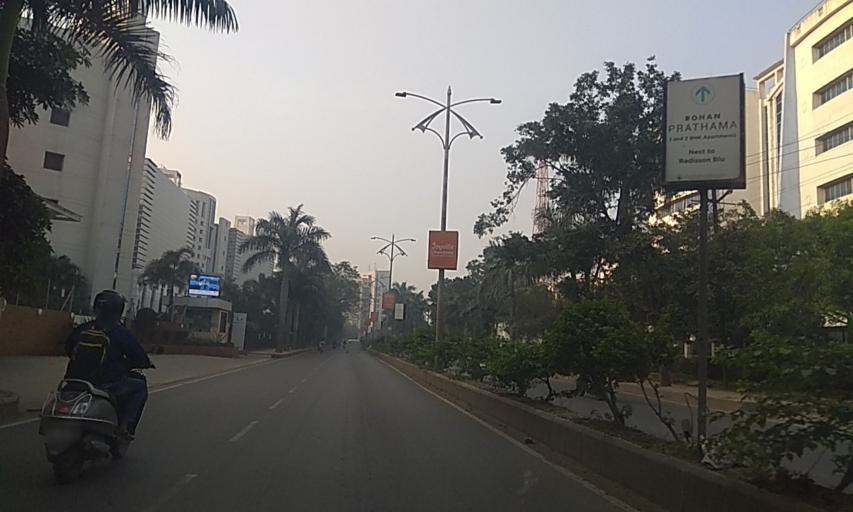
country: IN
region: Maharashtra
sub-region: Pune Division
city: Pimpri
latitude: 18.5889
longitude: 73.7379
